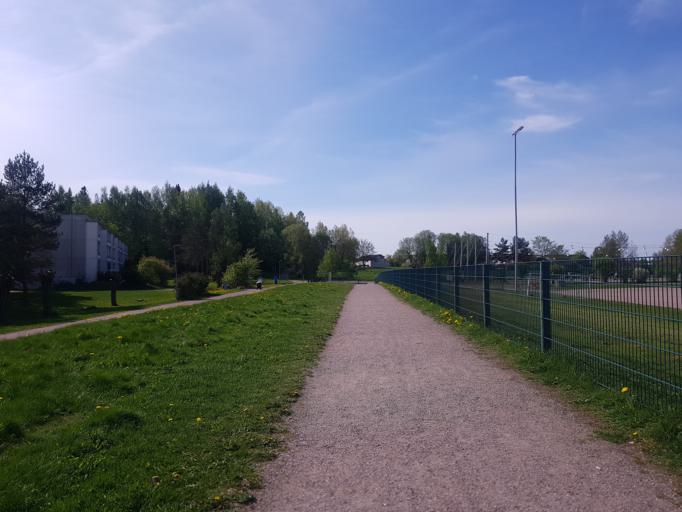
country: FI
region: Uusimaa
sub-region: Helsinki
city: Vantaa
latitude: 60.2743
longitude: 24.9837
